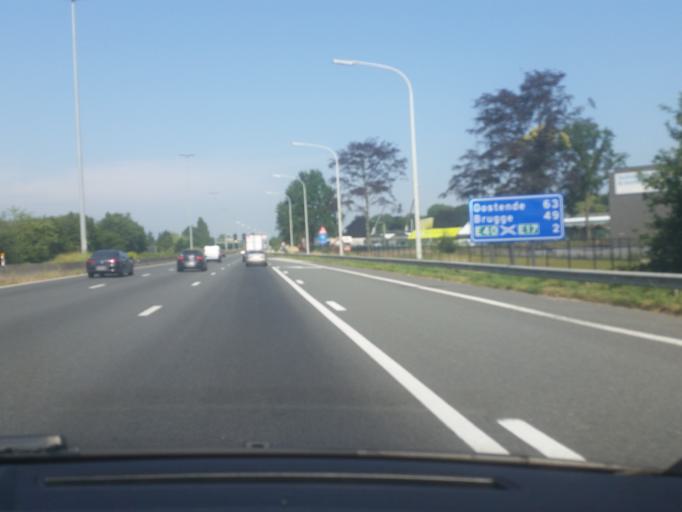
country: BE
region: Flanders
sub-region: Provincie Oost-Vlaanderen
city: Merelbeke
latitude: 51.0012
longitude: 3.7626
